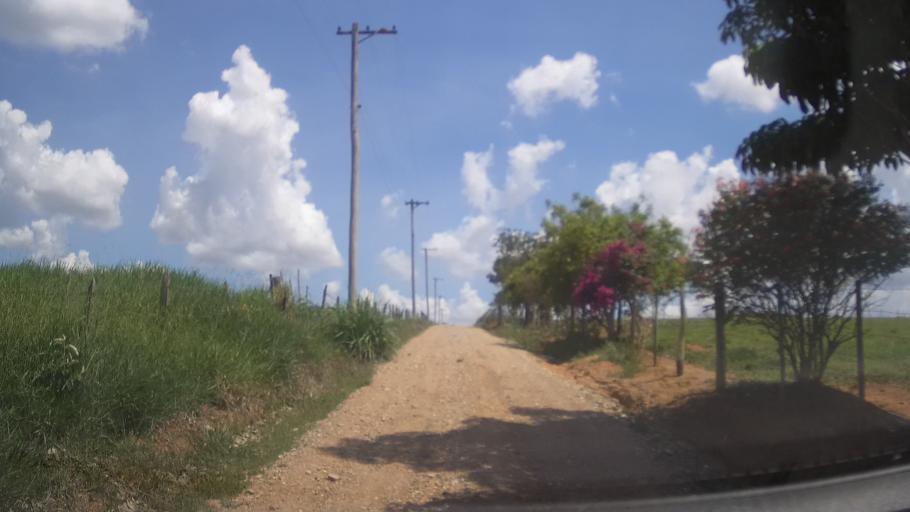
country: BR
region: Sao Paulo
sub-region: Jarinu
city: Jarinu
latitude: -23.1222
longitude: -46.7995
